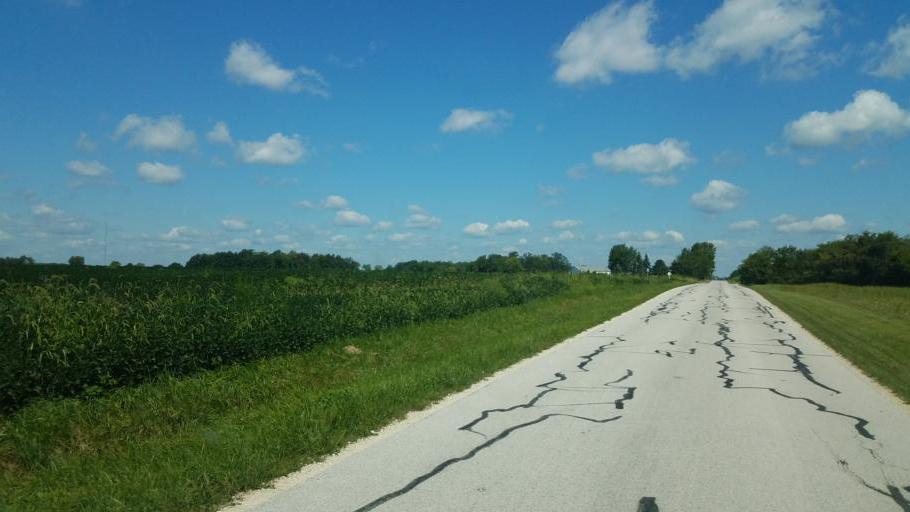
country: US
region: Ohio
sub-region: Wyandot County
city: Carey
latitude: 41.0618
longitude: -83.3246
